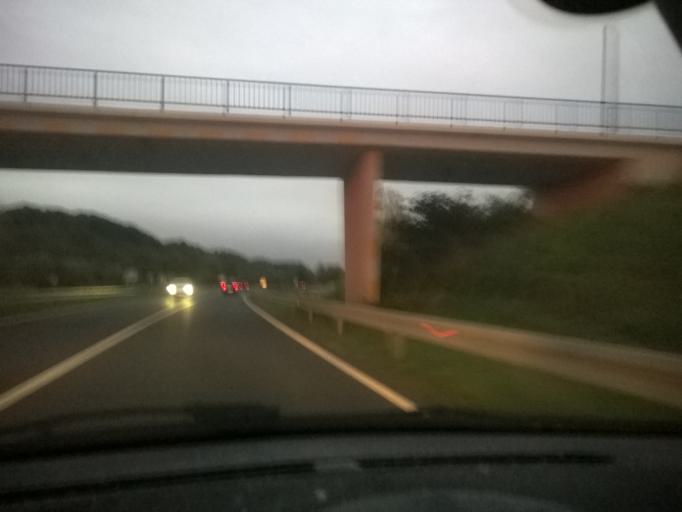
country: HR
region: Zagrebacka
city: Jakovlje
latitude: 45.9567
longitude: 15.8283
